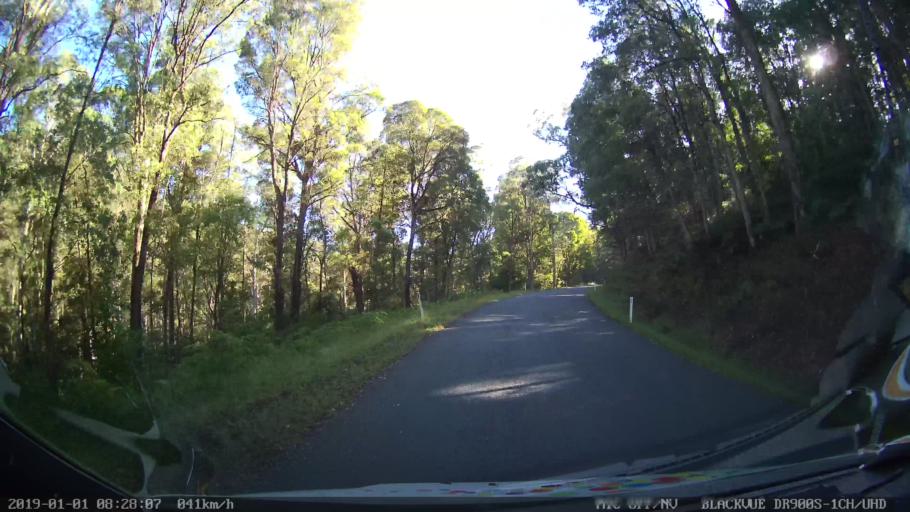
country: AU
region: New South Wales
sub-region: Snowy River
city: Jindabyne
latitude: -36.3778
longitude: 148.1877
